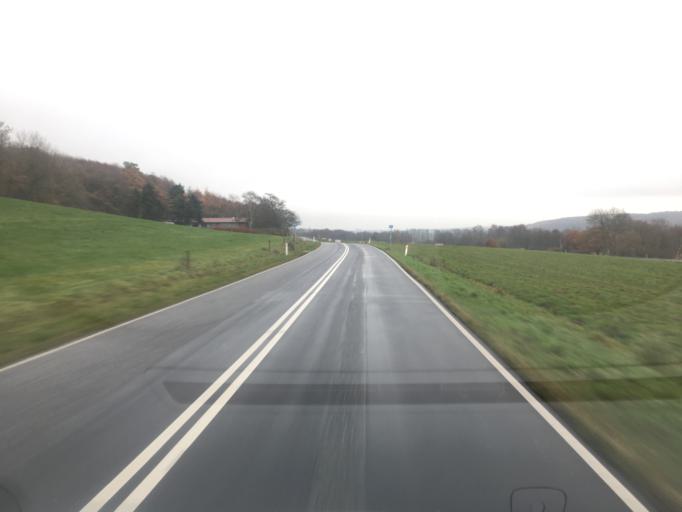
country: DK
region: Central Jutland
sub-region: Randers Kommune
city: Assentoft
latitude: 56.3942
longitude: 10.1682
